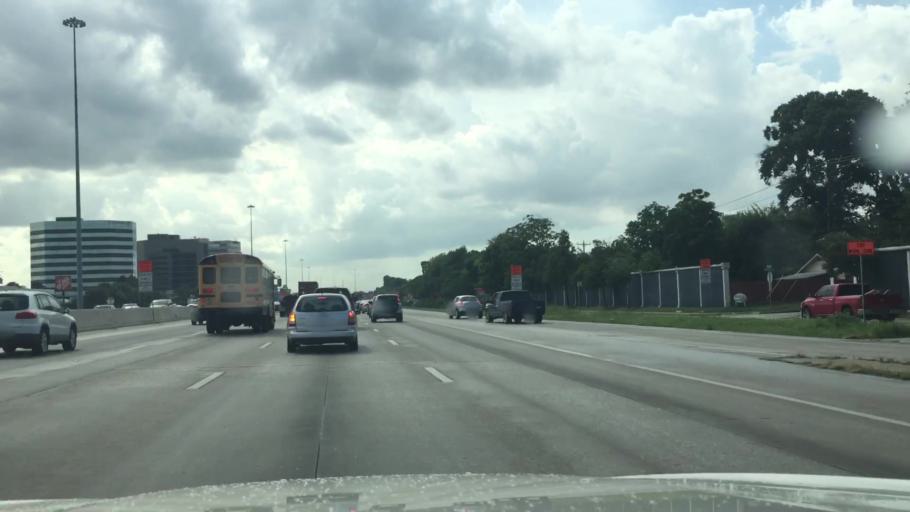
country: US
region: Texas
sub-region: Harris County
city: Houston
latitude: 29.8105
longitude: -95.4136
